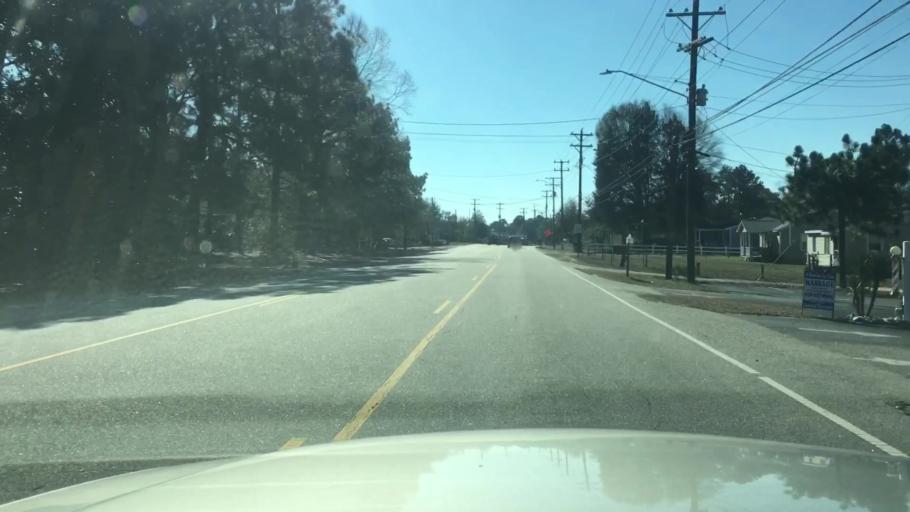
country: US
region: North Carolina
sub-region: Cumberland County
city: Hope Mills
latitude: 35.0180
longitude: -78.9352
